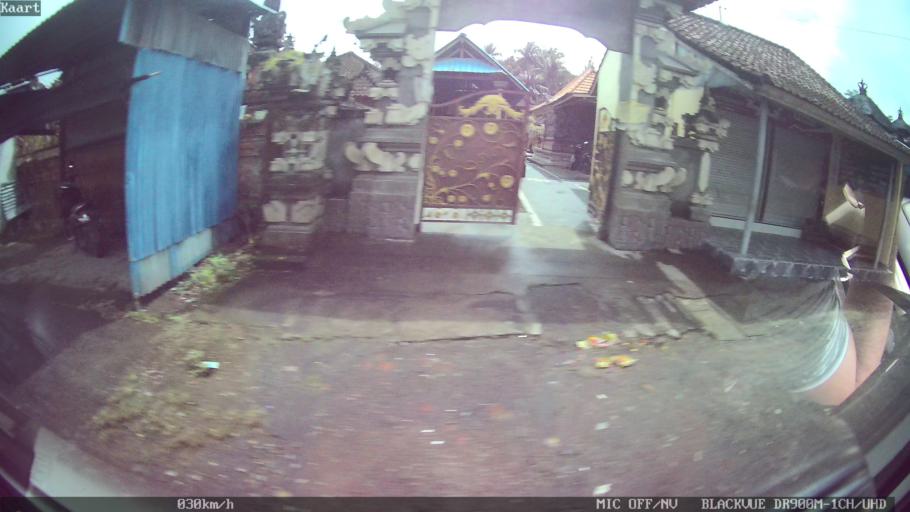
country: ID
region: Bali
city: Pegongan
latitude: -8.4833
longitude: 115.2272
